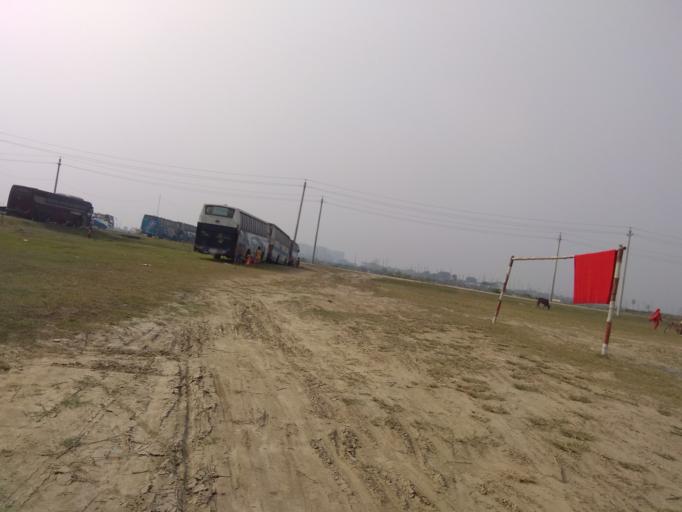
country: BD
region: Dhaka
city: Tungi
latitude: 23.8564
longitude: 90.3730
